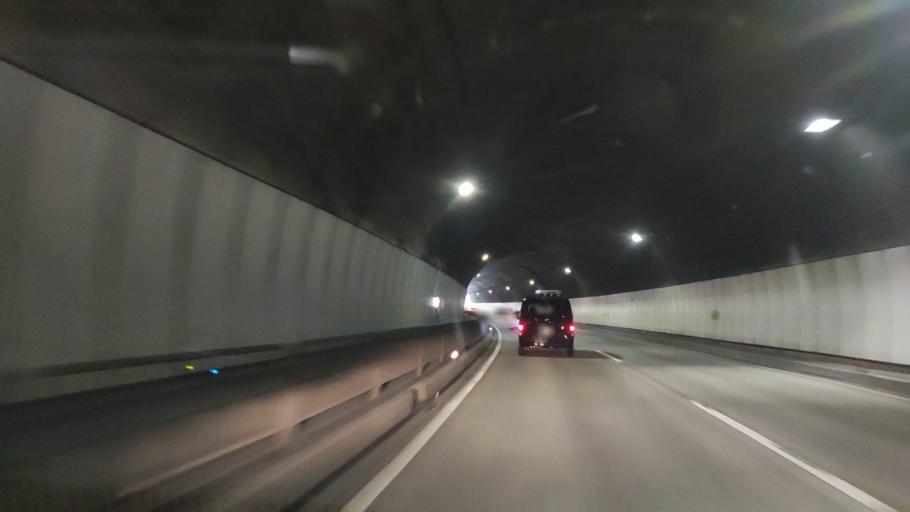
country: JP
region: Hyogo
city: Nishiwaki
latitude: 34.9718
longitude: 134.9762
